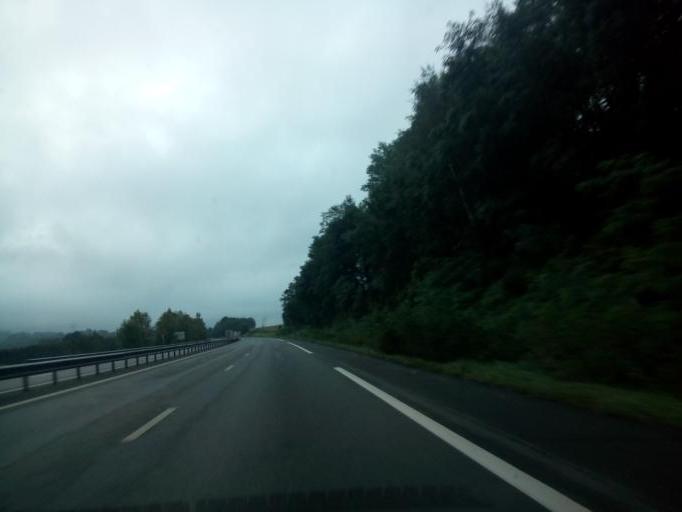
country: FR
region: Rhone-Alpes
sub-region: Departement de la Savoie
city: Le Pont-de-Beauvoisin
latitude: 45.5664
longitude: 5.6744
